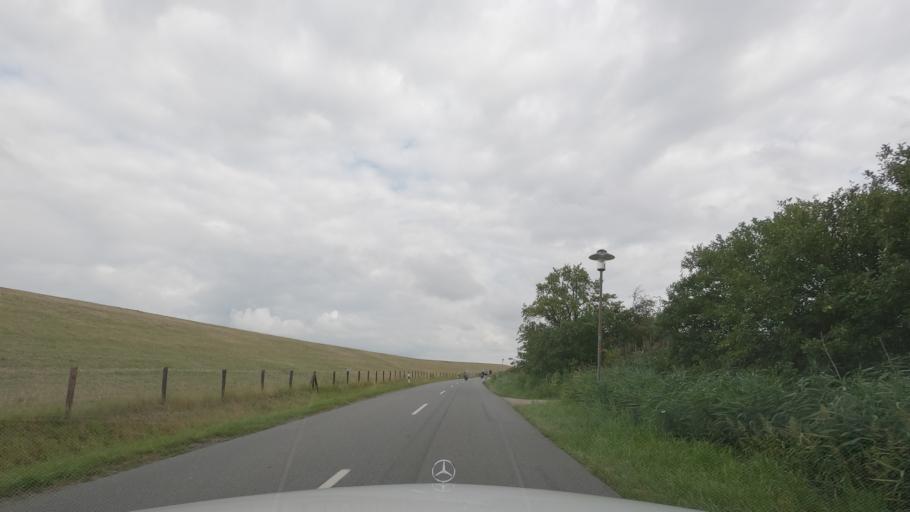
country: DE
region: Lower Saxony
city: Brake (Unterweser)
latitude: 53.3049
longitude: 8.5278
